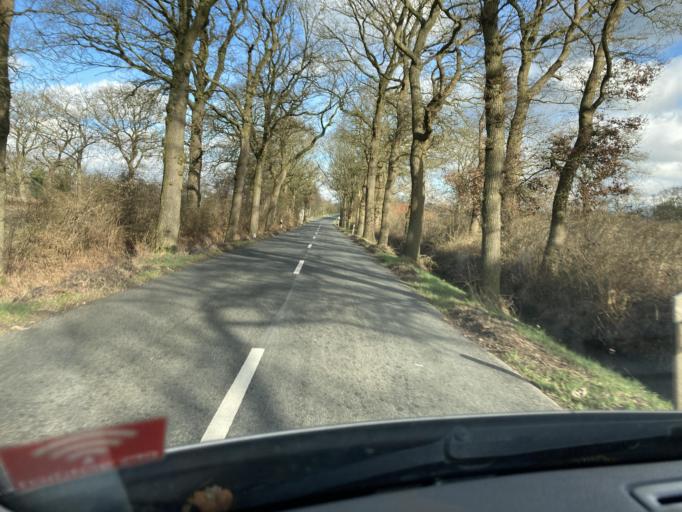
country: DE
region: Lower Saxony
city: Filsum
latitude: 53.2426
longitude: 7.6655
